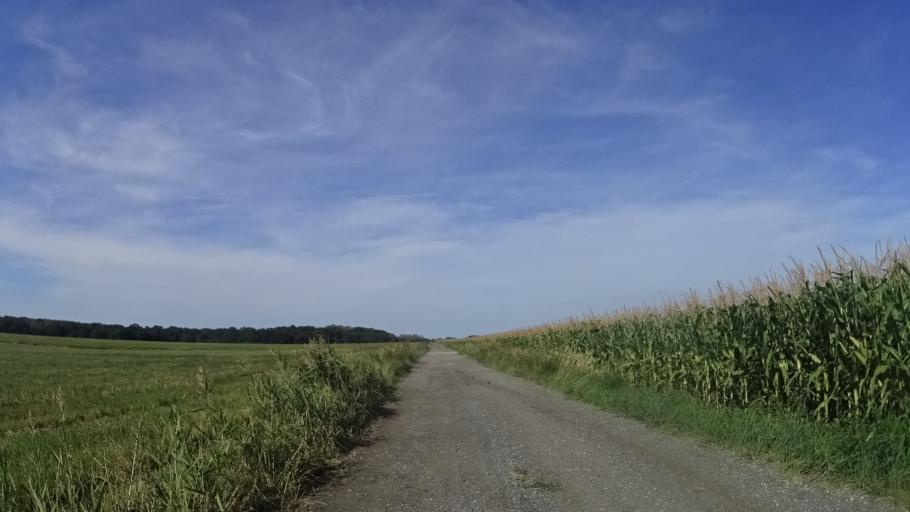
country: AT
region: Lower Austria
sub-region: Politischer Bezirk Ganserndorf
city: Durnkrut
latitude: 48.4512
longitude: 16.8860
